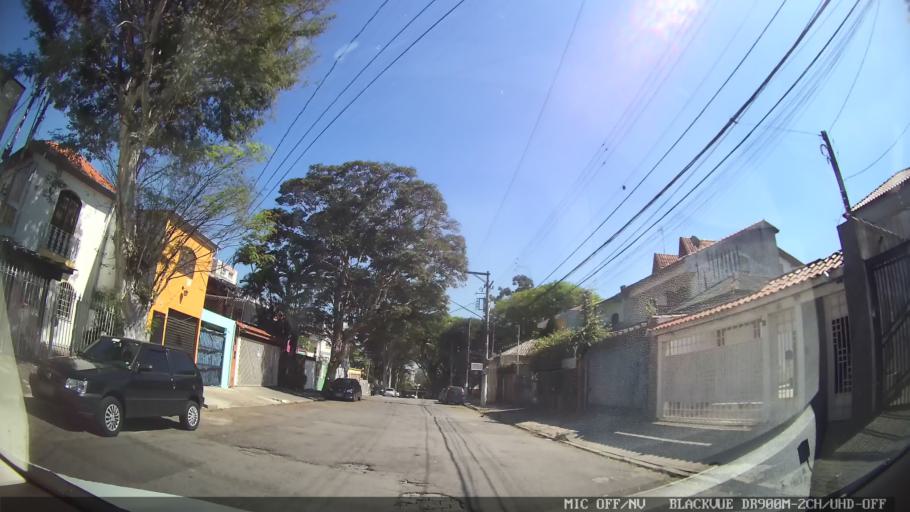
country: BR
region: Sao Paulo
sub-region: Sao Paulo
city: Sao Paulo
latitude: -23.5093
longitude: -46.6561
